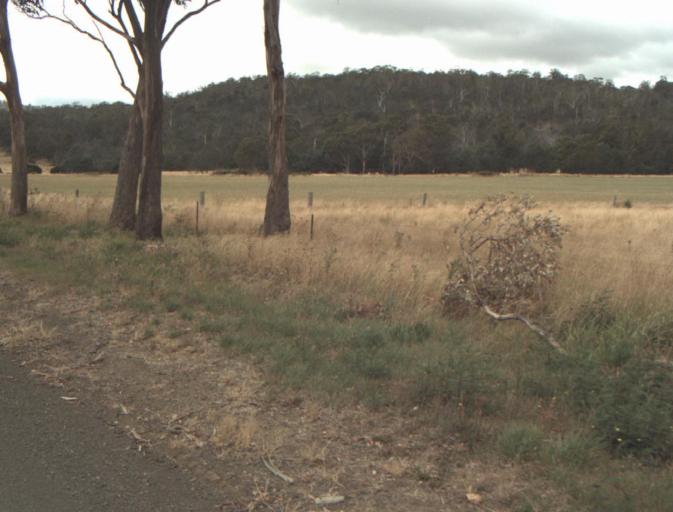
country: AU
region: Tasmania
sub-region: Northern Midlands
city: Evandale
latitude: -41.5257
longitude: 147.3622
